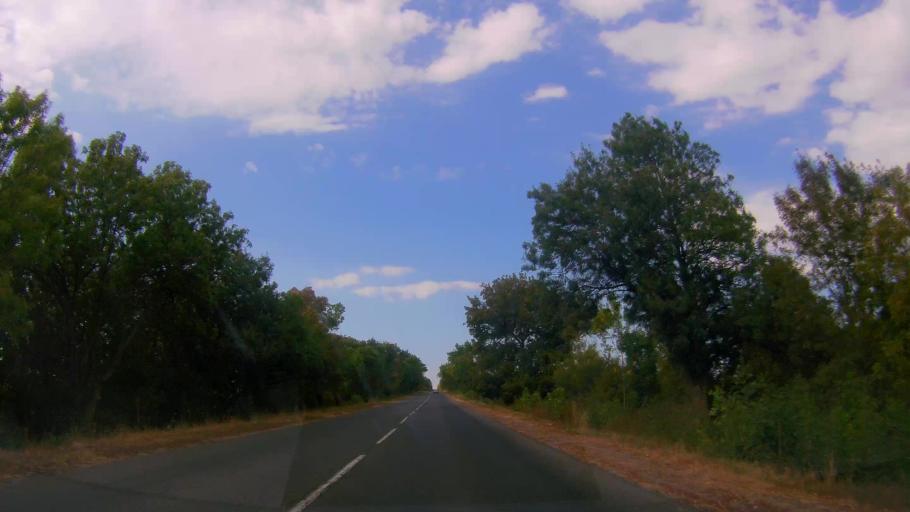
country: BG
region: Burgas
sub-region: Obshtina Aytos
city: Aytos
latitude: 42.6905
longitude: 27.1602
